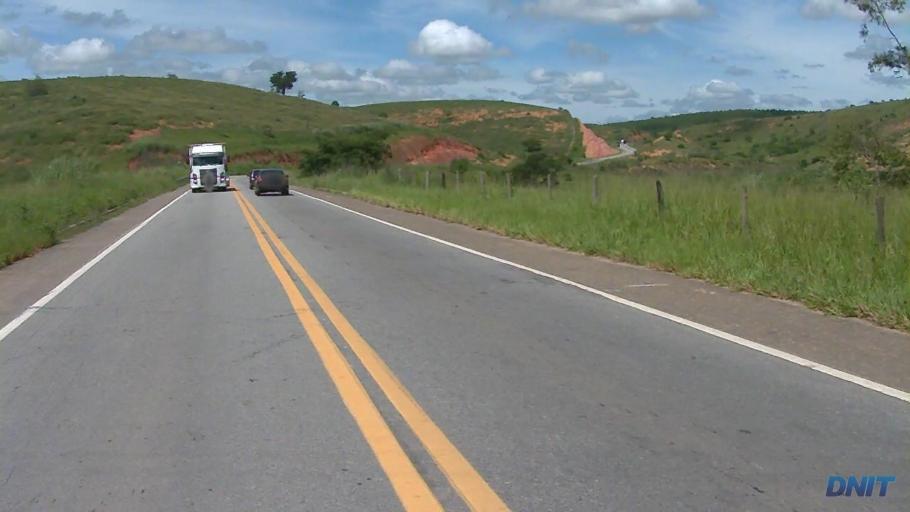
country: BR
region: Minas Gerais
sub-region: Governador Valadares
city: Governador Valadares
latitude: -19.0593
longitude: -42.1607
